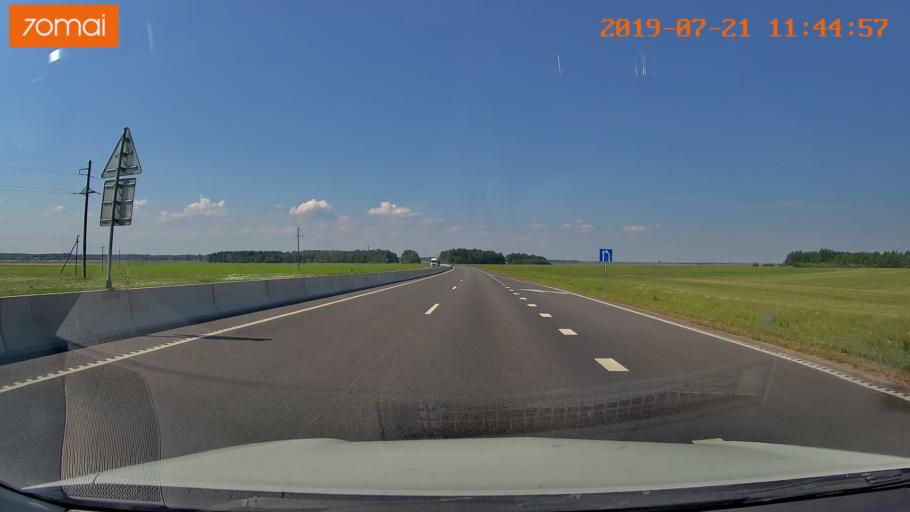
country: BY
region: Grodnenskaya
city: Lyubcha
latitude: 53.9141
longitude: 26.0775
